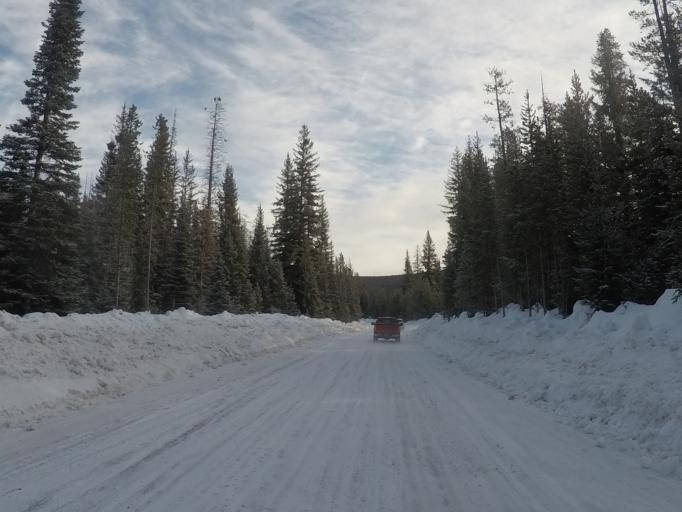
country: US
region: Montana
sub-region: Granite County
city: Philipsburg
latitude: 46.2454
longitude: -113.2433
